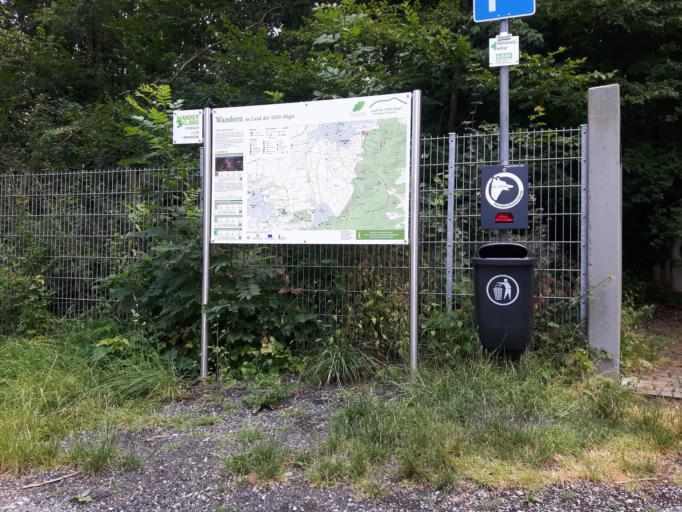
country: DE
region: Baden-Wuerttemberg
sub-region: Regierungsbezirk Stuttgart
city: Eppingen
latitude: 49.1308
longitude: 8.9327
